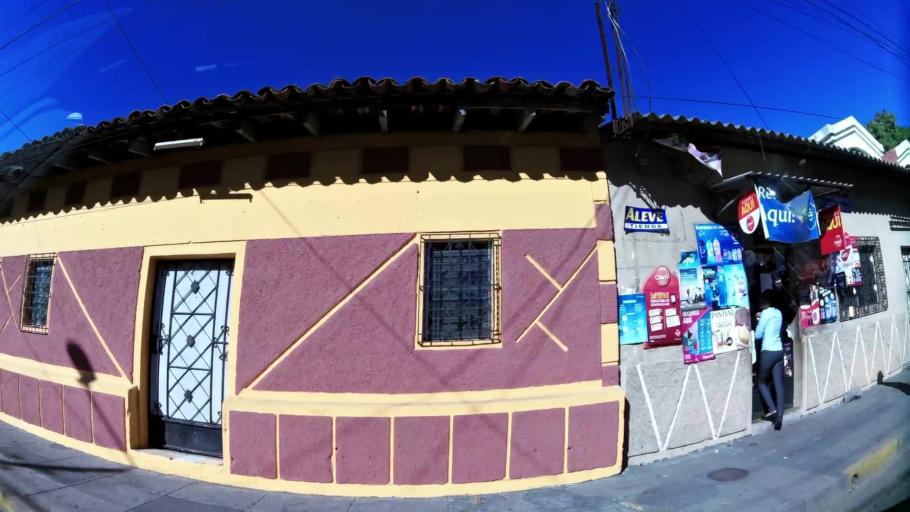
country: SV
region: San Miguel
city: San Miguel
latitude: 13.4718
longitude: -88.1771
